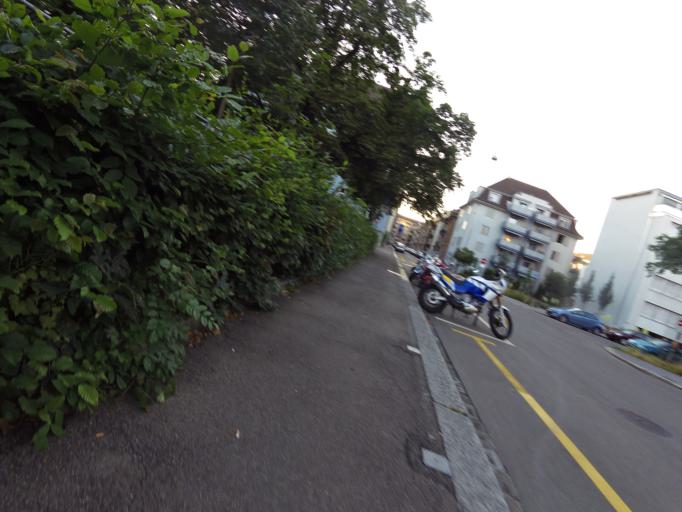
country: CH
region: Zurich
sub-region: Bezirk Zuerich
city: Zuerich (Kreis 4) / Werd
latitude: 47.3688
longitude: 8.5231
